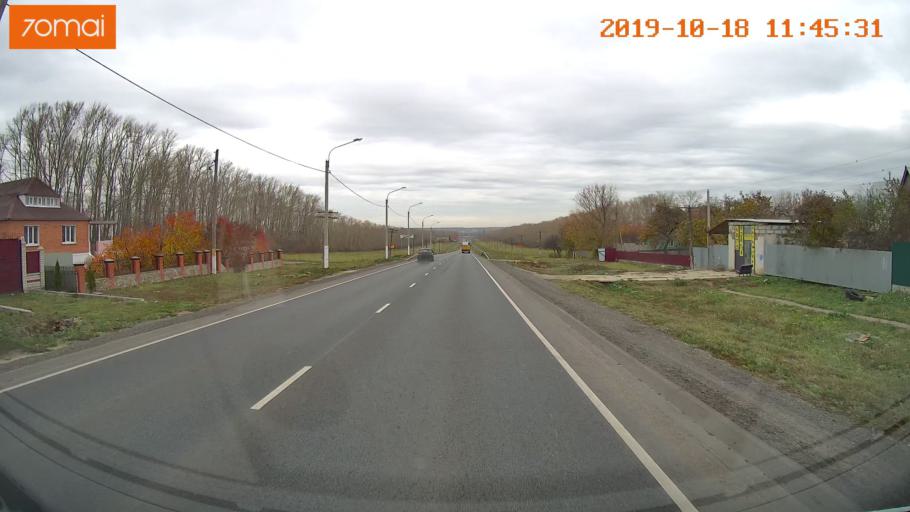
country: RU
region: Rjazan
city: Mikhaylov
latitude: 54.2112
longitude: 38.9711
